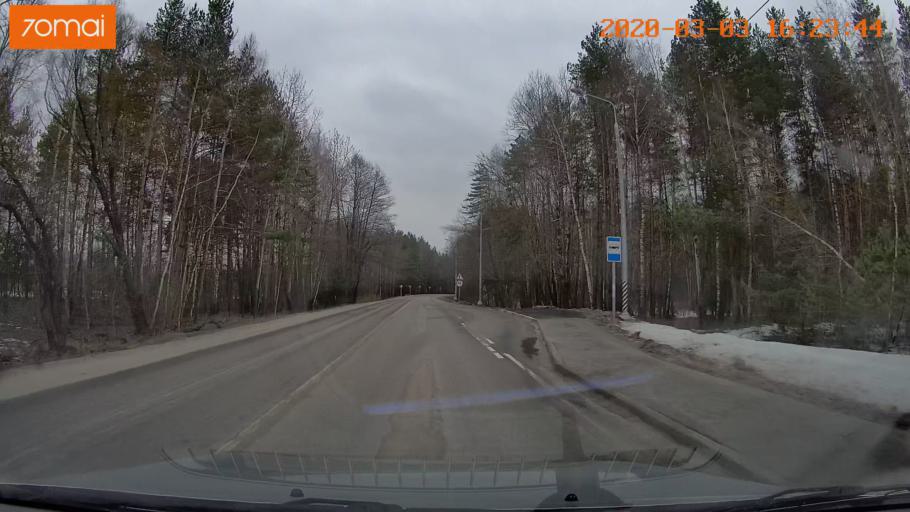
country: RU
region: Moskovskaya
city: Imeni Tsyurupy
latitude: 55.4769
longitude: 38.6563
